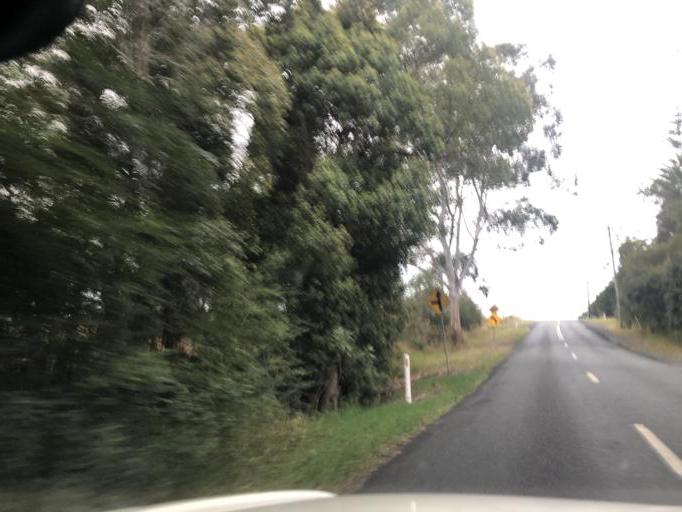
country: AU
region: New South Wales
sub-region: Coffs Harbour
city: Coffs Harbour
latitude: -30.2568
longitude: 153.0361
